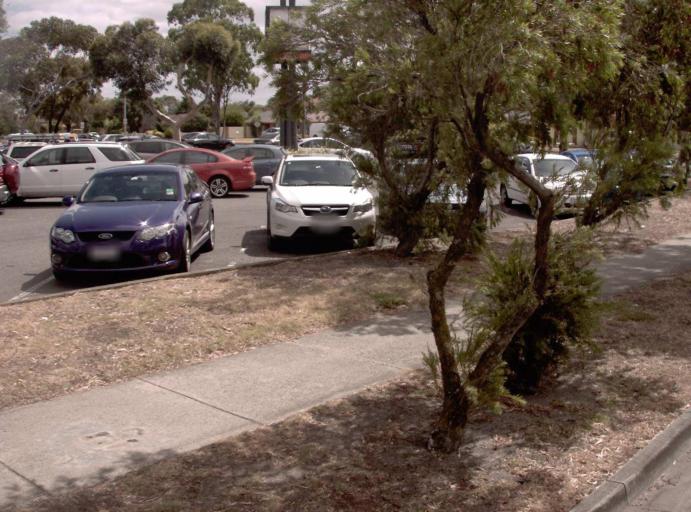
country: AU
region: Victoria
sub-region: Kingston
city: Patterson Lakes
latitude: -38.0681
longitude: 145.1444
